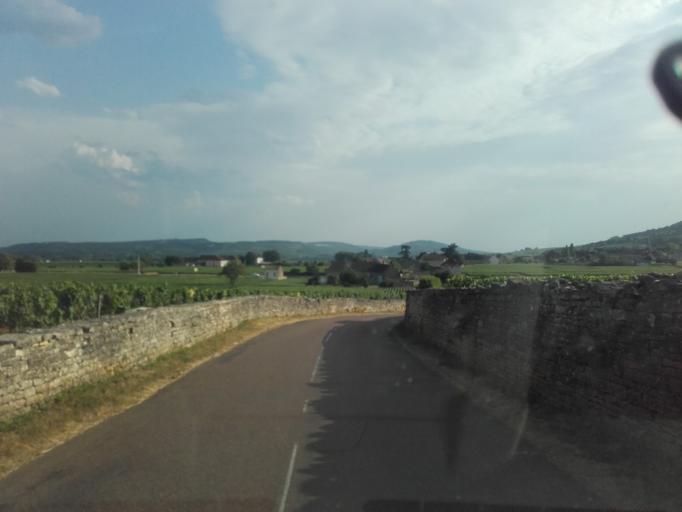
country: FR
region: Bourgogne
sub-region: Departement de la Cote-d'Or
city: Corpeau
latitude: 46.9427
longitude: 4.7374
